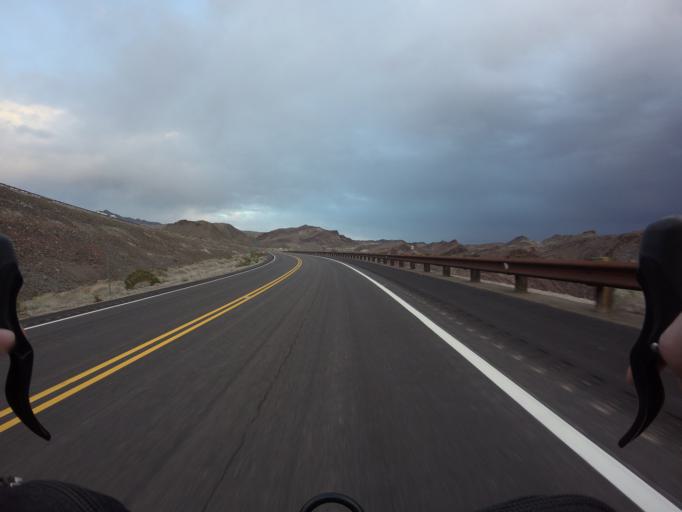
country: US
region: Nevada
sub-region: Clark County
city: Boulder City
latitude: 36.0079
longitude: -114.7290
